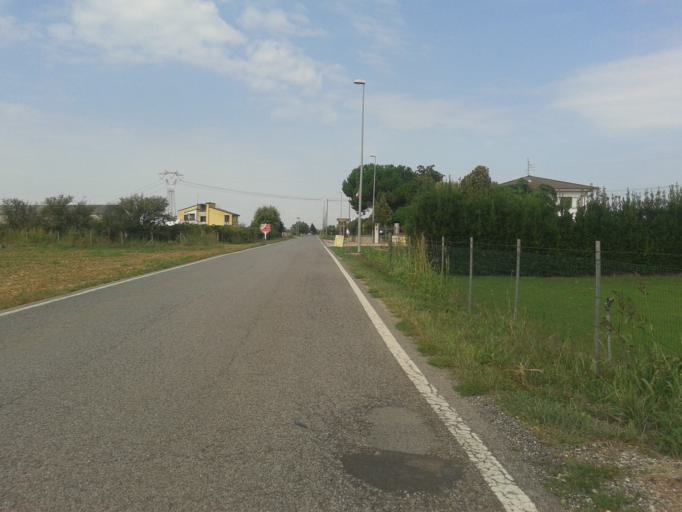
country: IT
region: Veneto
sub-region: Provincia di Verona
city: Mozzecane
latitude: 45.3160
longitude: 10.8021
